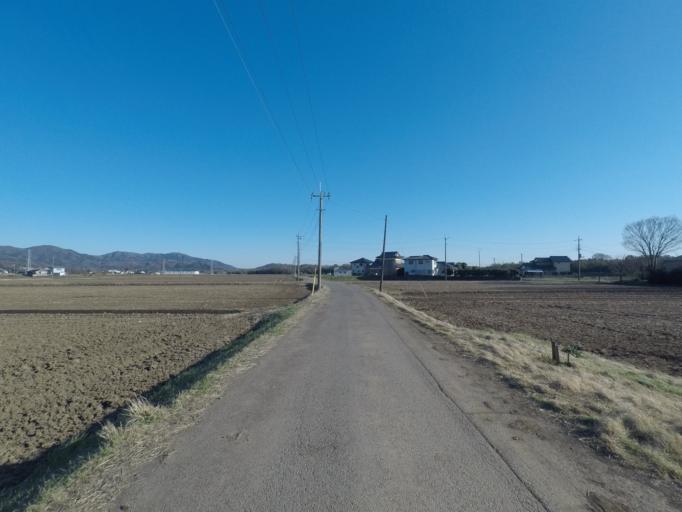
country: JP
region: Ibaraki
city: Tsukuba
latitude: 36.2151
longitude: 140.0630
